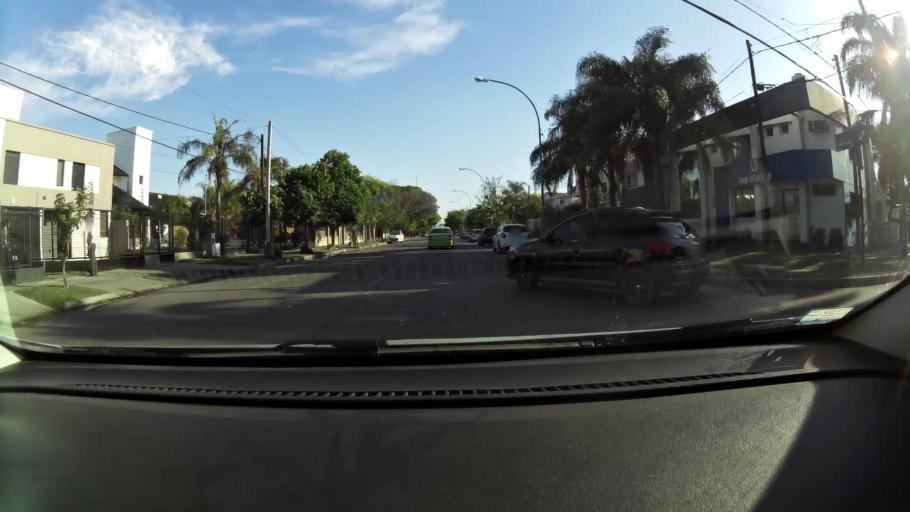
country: AR
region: Cordoba
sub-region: Departamento de Capital
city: Cordoba
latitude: -31.3704
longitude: -64.2265
